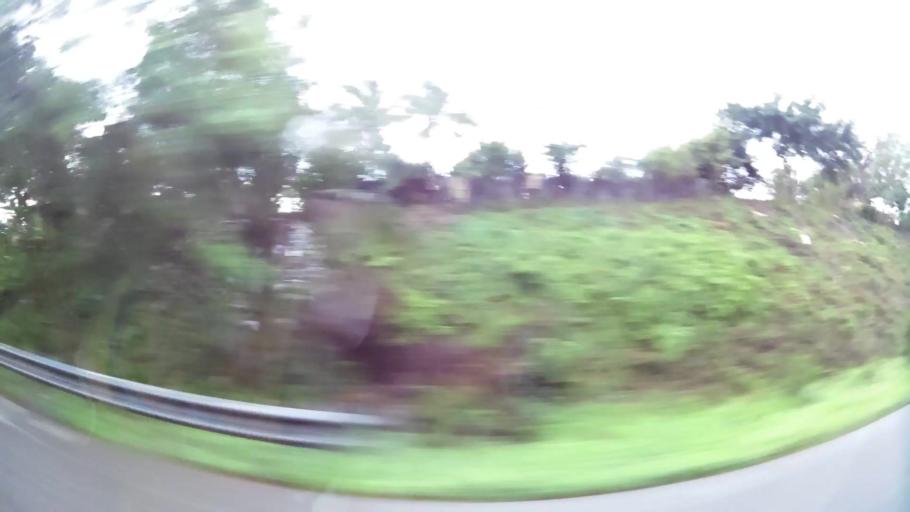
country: DO
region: San Cristobal
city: Villa Altagracia
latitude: 18.5996
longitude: -70.1338
